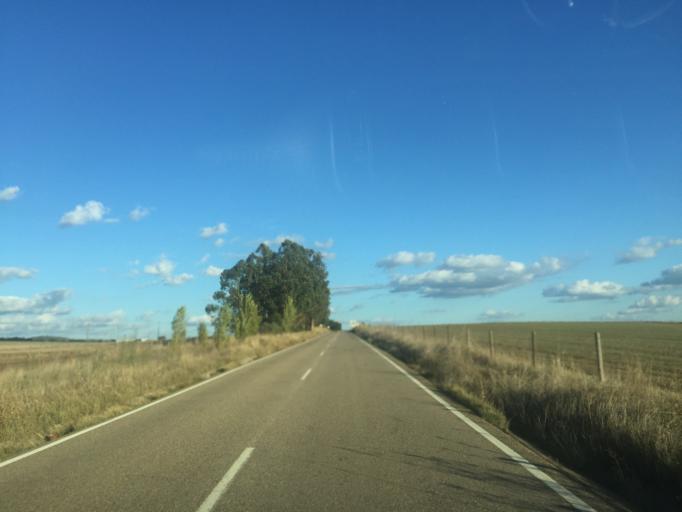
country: PT
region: Portalegre
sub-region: Alter do Chao
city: Alter do Chao
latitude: 39.1985
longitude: -7.7125
